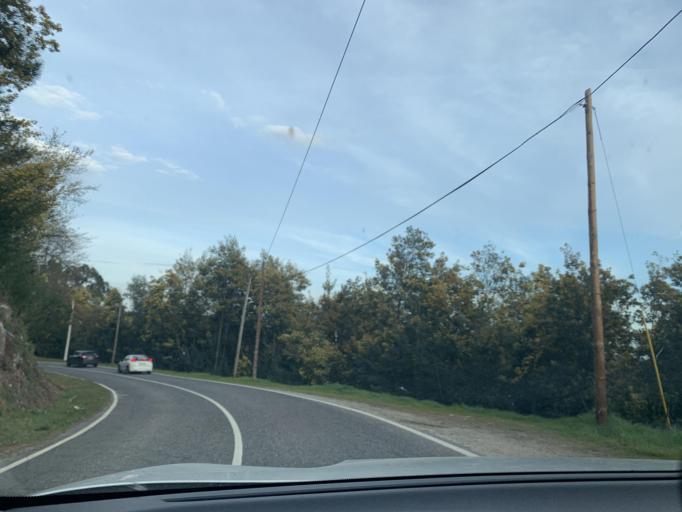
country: PT
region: Viseu
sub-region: Viseu
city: Viseu
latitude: 40.5943
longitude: -7.9968
